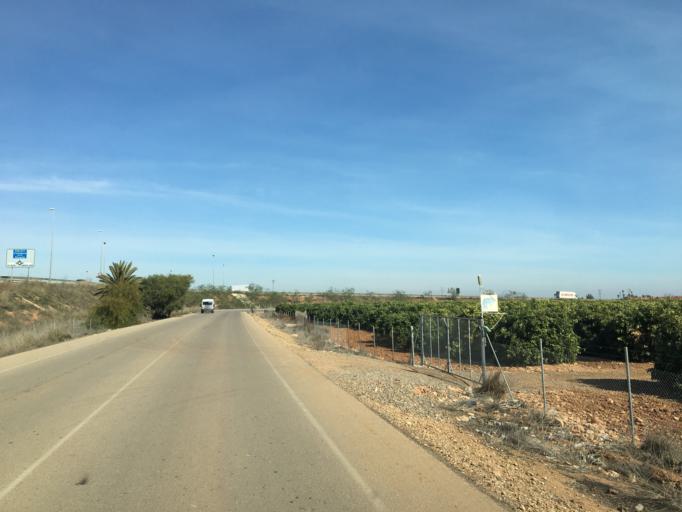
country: ES
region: Murcia
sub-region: Murcia
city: Cartagena
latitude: 37.6616
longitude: -1.0243
